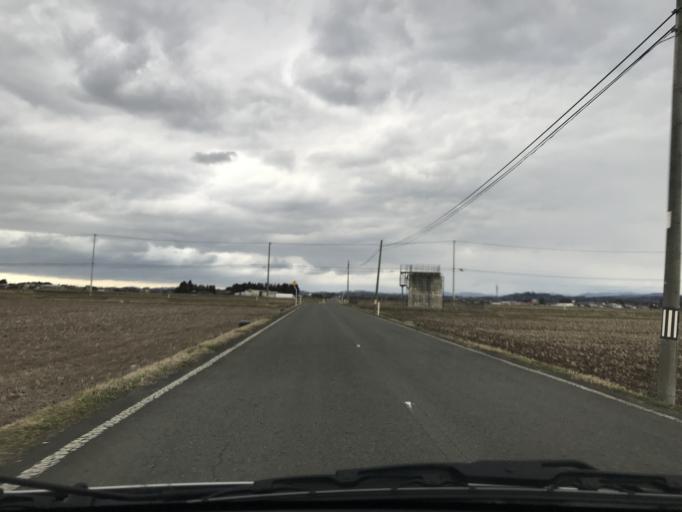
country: JP
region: Iwate
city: Mizusawa
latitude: 39.1055
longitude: 141.1629
